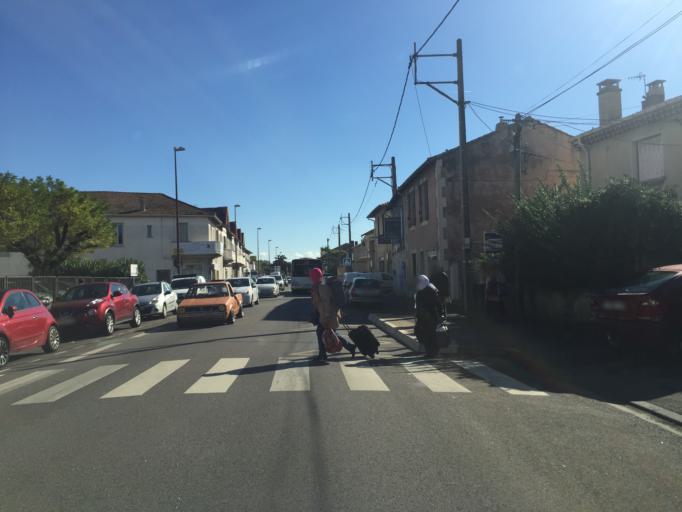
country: FR
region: Provence-Alpes-Cote d'Azur
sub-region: Departement du Vaucluse
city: Avignon
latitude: 43.9417
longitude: 4.8241
